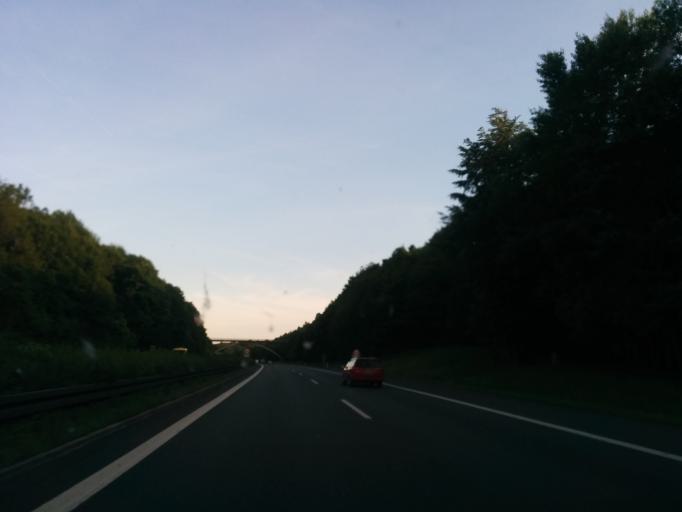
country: DE
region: Bavaria
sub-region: Regierungsbezirk Unterfranken
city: Arnstein
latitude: 49.9271
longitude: 9.9981
